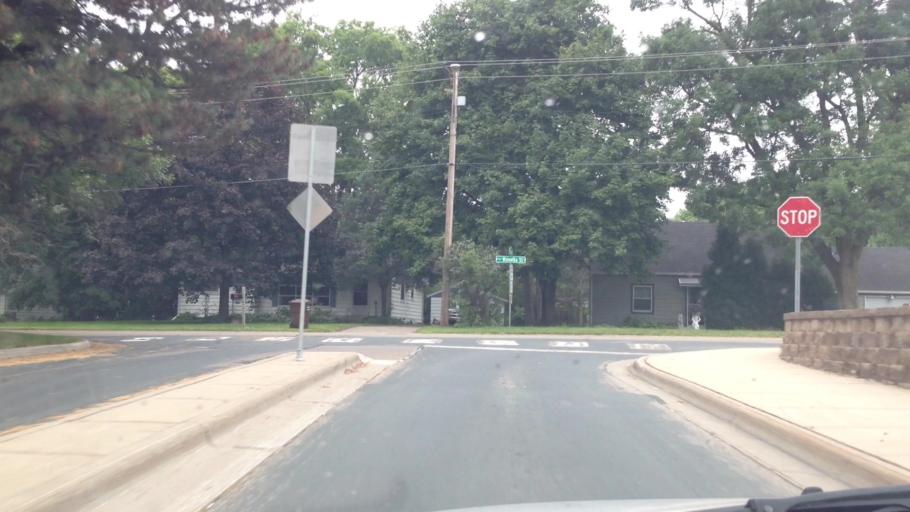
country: US
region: Minnesota
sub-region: Hennepin County
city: Saint Louis Park
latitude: 44.9747
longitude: -93.3806
